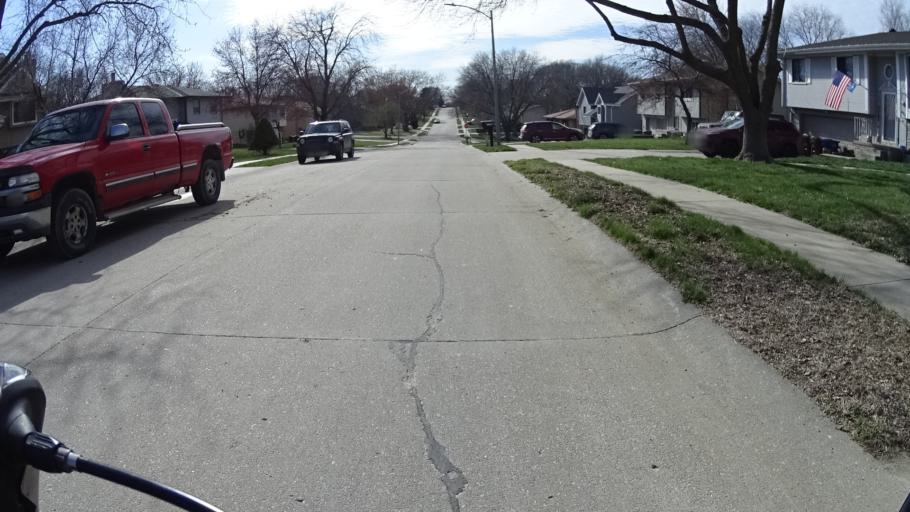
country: US
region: Nebraska
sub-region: Sarpy County
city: Offutt Air Force Base
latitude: 41.1142
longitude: -95.9590
